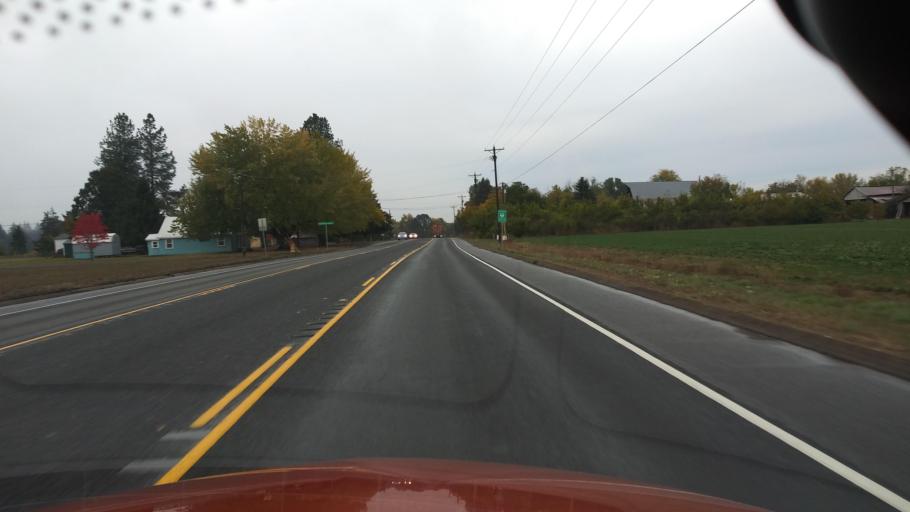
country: US
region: Oregon
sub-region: Washington County
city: Cornelius
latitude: 45.5593
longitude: -123.0578
